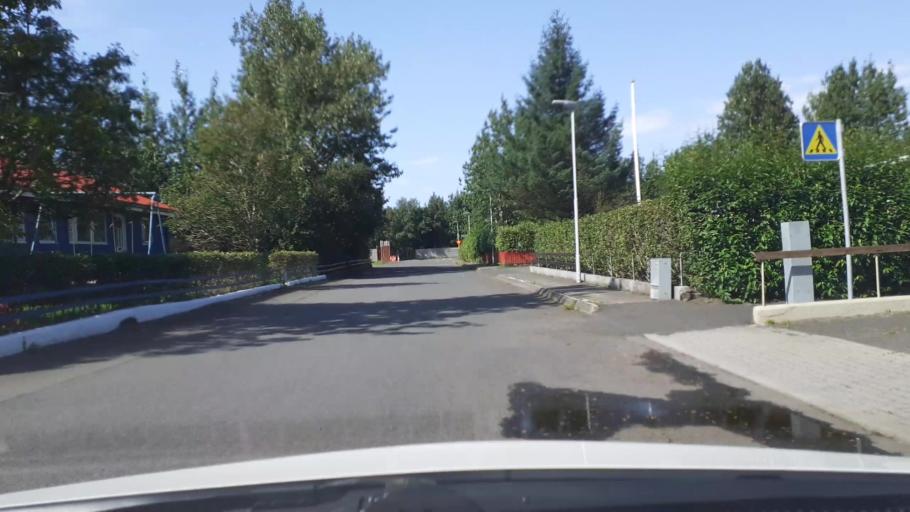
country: IS
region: South
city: Selfoss
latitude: 63.9295
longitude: -21.0094
